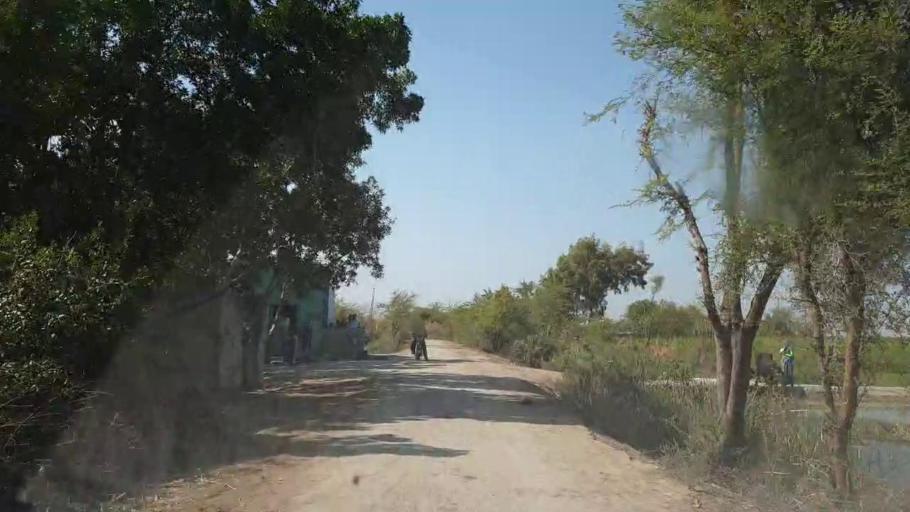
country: PK
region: Sindh
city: Mirpur Khas
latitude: 25.7352
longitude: 69.1076
